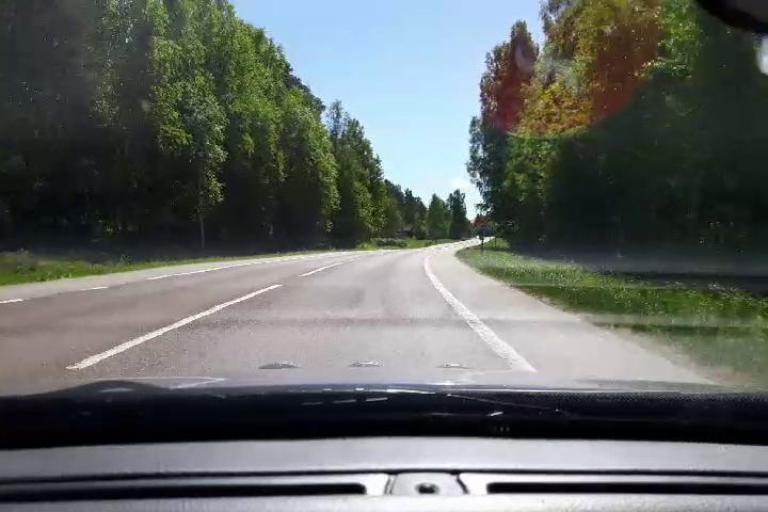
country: SE
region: Jaemtland
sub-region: Harjedalens Kommun
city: Sveg
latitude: 62.1702
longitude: 14.9513
